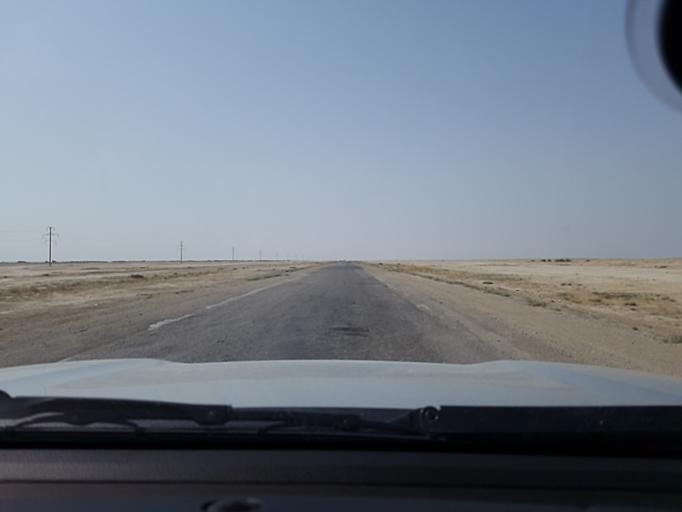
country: TM
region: Balkan
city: Gumdag
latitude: 38.8497
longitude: 54.5954
